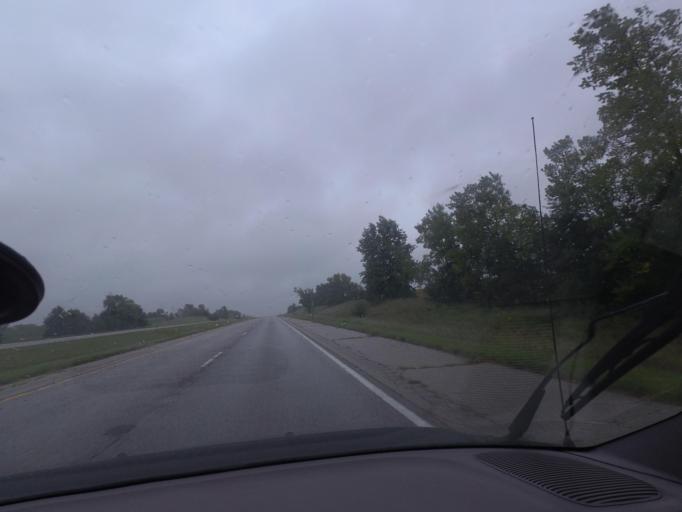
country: US
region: Illinois
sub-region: Pike County
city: Pittsfield
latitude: 39.6839
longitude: -90.8780
